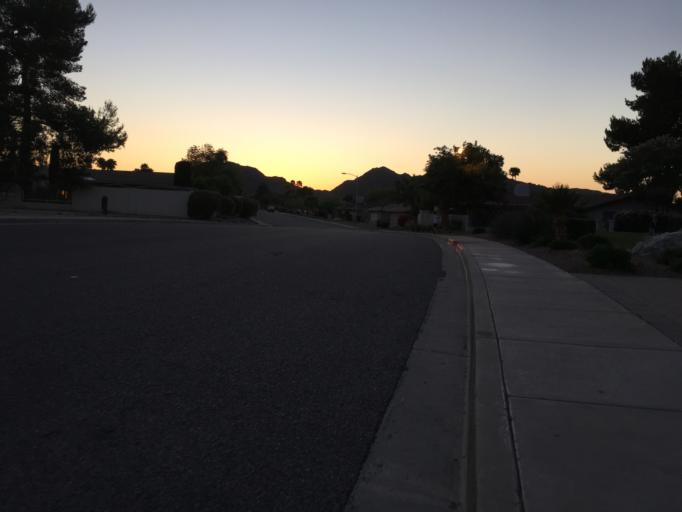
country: US
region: Arizona
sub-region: Maricopa County
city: Paradise Valley
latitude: 33.5708
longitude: -112.0152
